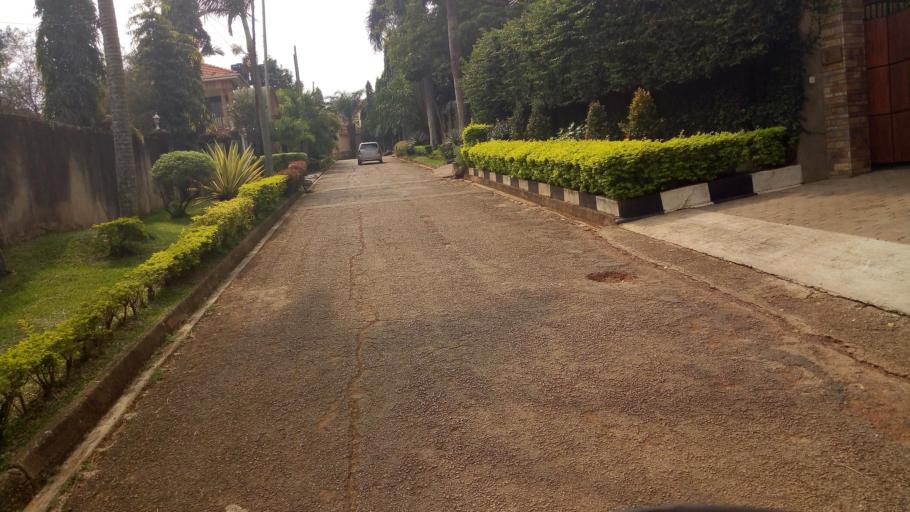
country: UG
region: Central Region
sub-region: Kampala District
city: Kampala
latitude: 0.3102
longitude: 32.6230
